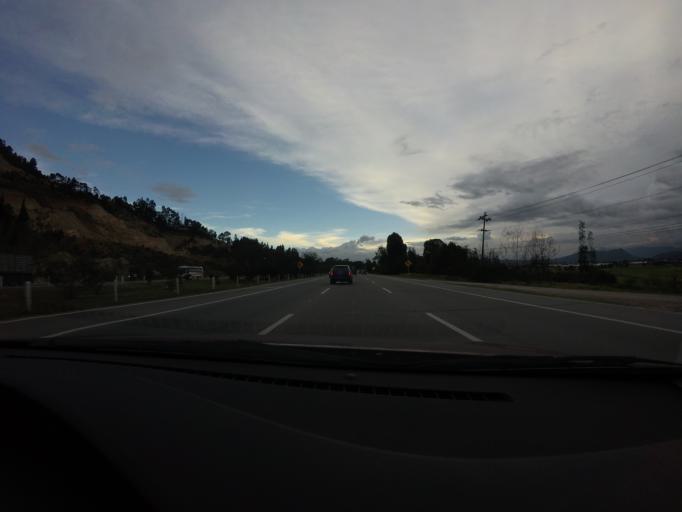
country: CO
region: Cundinamarca
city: Cajica
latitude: 4.9278
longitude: -73.9951
